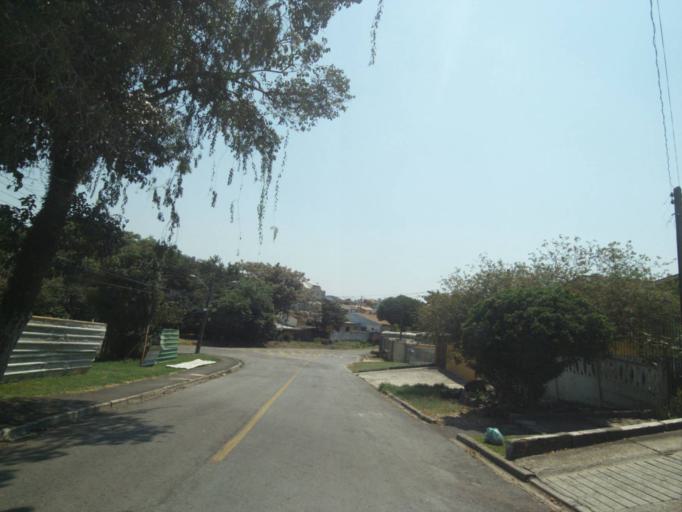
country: BR
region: Parana
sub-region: Sao Jose Dos Pinhais
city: Sao Jose dos Pinhais
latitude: -25.5078
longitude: -49.2686
